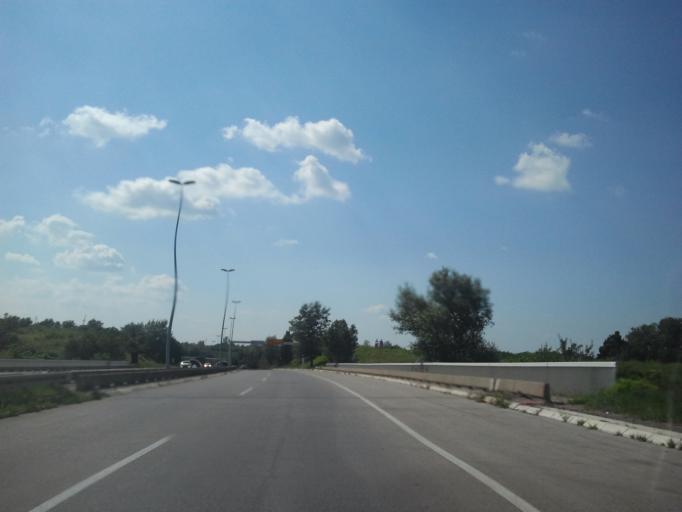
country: RS
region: Autonomna Pokrajina Vojvodina
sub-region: Juznobacki Okrug
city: Petrovaradin
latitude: 45.2274
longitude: 19.8654
